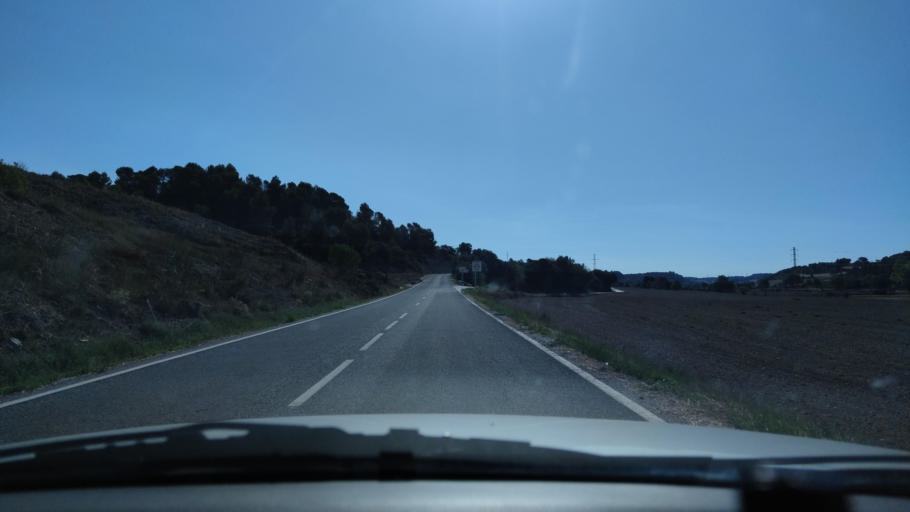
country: ES
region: Catalonia
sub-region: Provincia de Barcelona
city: Pujalt
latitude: 41.6957
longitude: 1.3513
